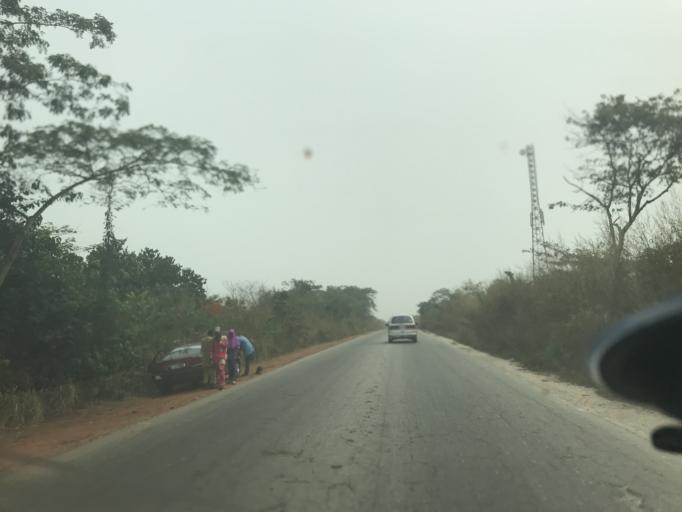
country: NG
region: Ogun
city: Ilaro
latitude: 6.8840
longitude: 3.1025
